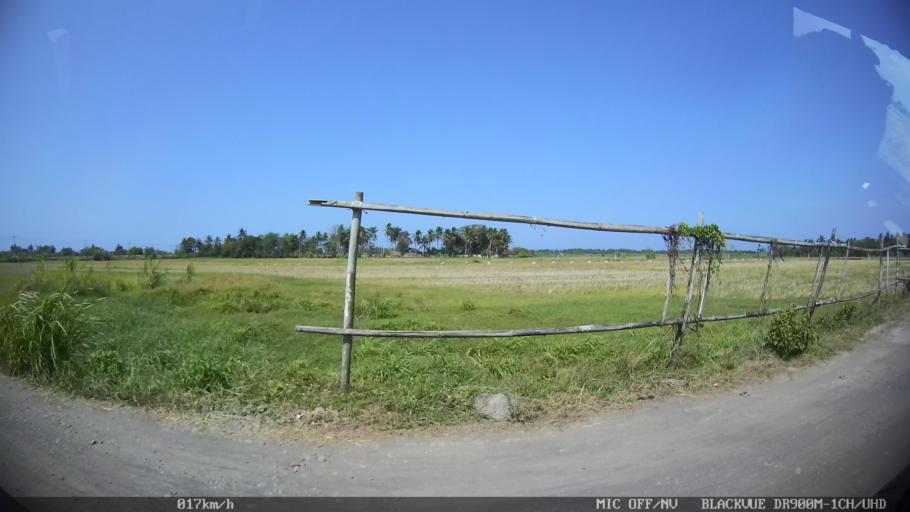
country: ID
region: Daerah Istimewa Yogyakarta
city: Srandakan
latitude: -7.9716
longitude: 110.2094
